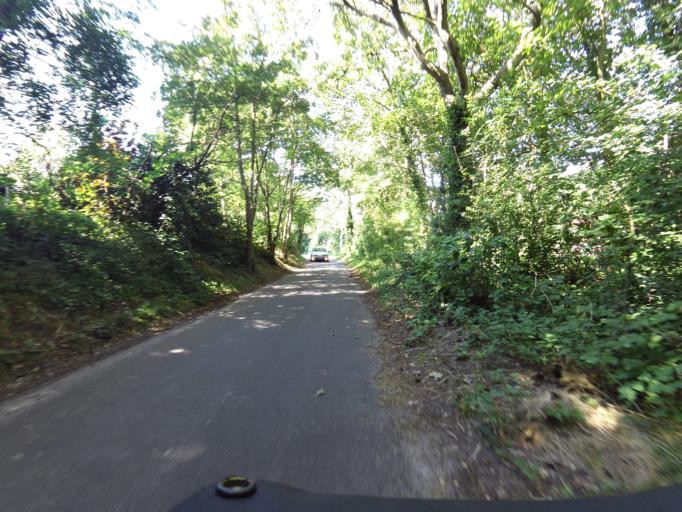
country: NL
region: Zeeland
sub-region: Schouwen-Duiveland
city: Renesse
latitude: 51.7378
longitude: 3.7677
